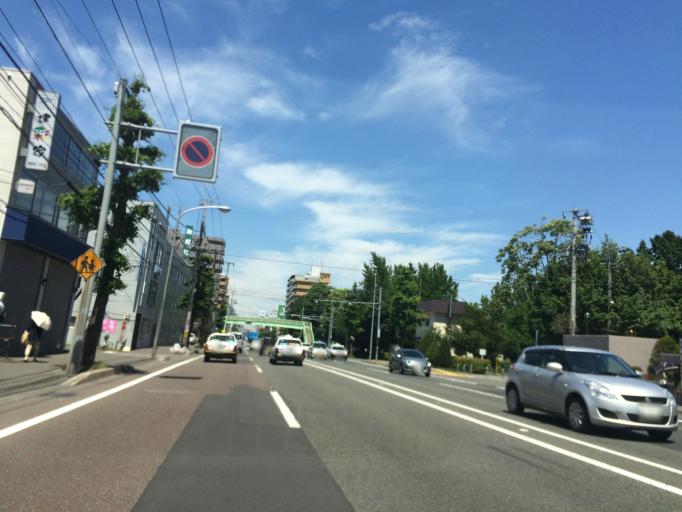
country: JP
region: Hokkaido
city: Sapporo
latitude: 43.0396
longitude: 141.3437
